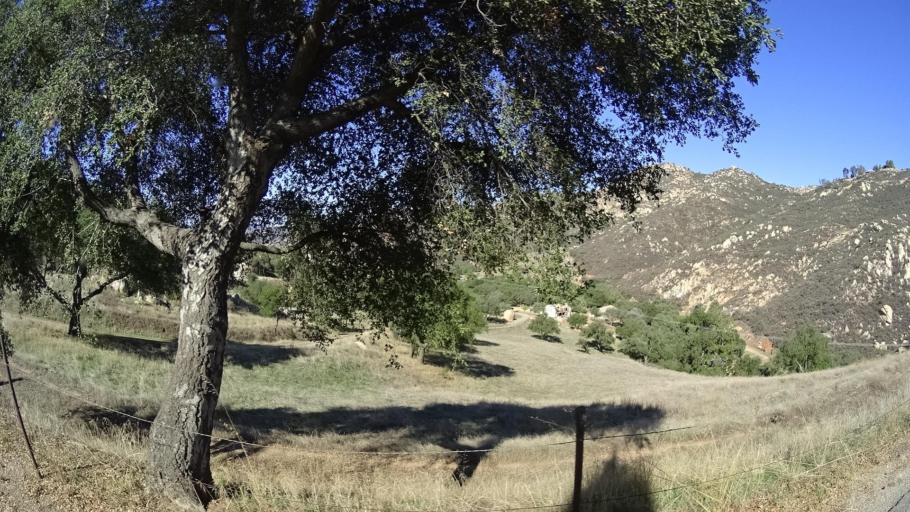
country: US
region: California
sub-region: San Diego County
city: Jamul
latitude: 32.7106
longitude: -116.7781
